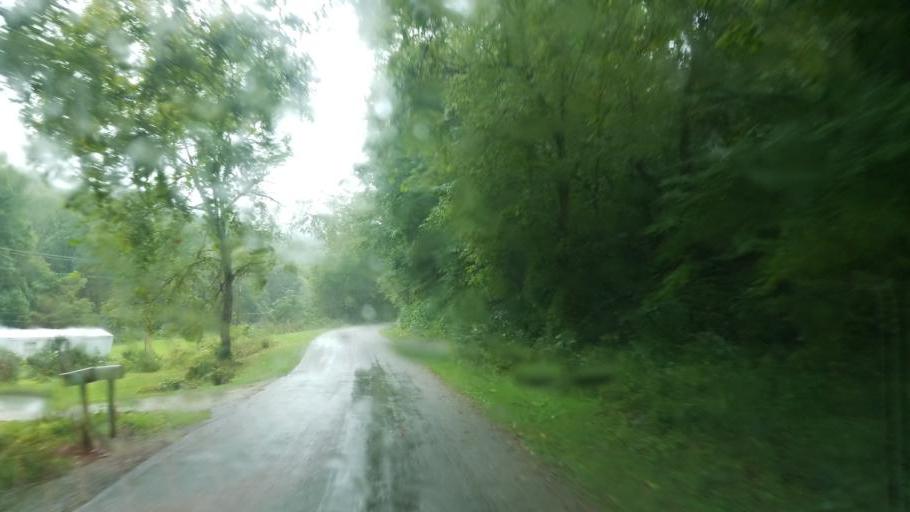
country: US
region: Kentucky
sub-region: Lewis County
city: Vanceburg
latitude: 38.7900
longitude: -83.2571
